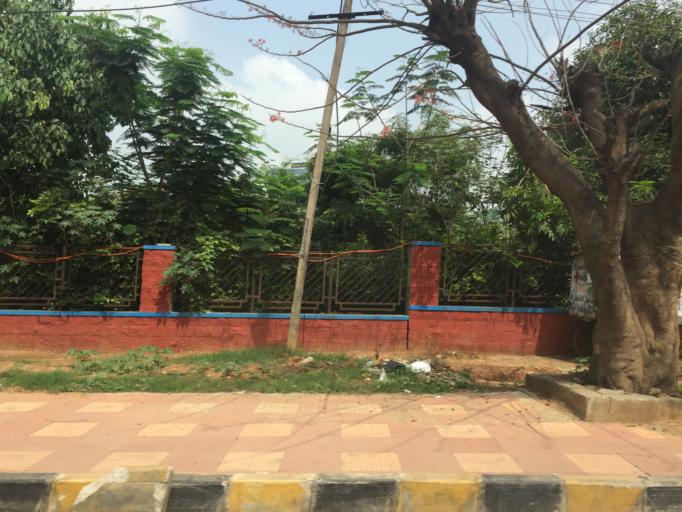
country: IN
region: Karnataka
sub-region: Bangalore Rural
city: Hoskote
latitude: 12.9779
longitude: 77.7272
